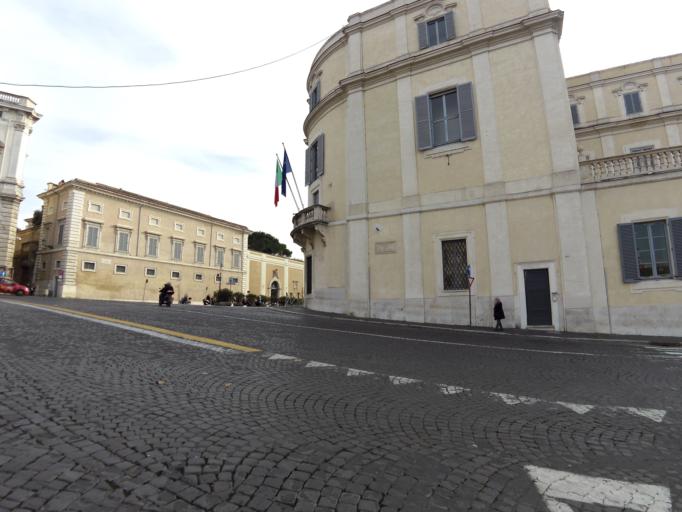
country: IT
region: Latium
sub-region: Citta metropolitana di Roma Capitale
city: Rome
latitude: 41.8990
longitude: 12.4863
